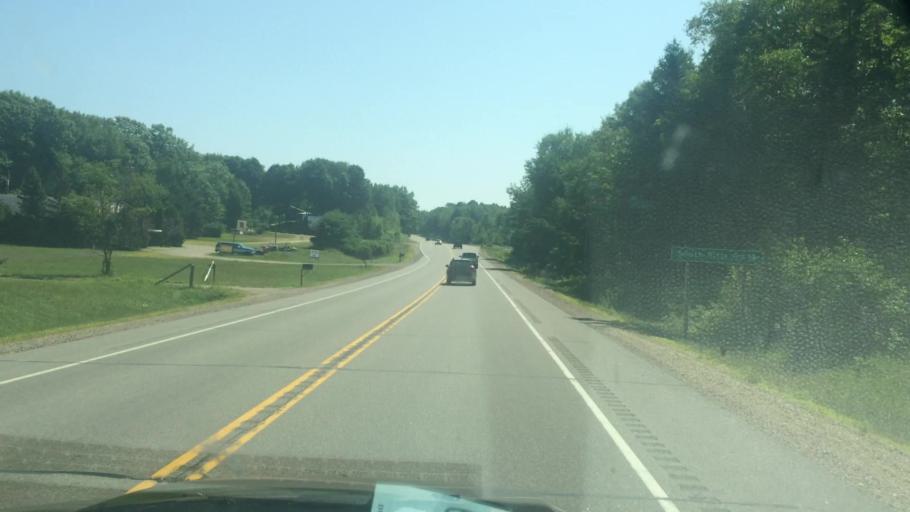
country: US
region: Wisconsin
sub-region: Oneida County
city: Rhinelander
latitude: 45.6164
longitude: -89.5088
